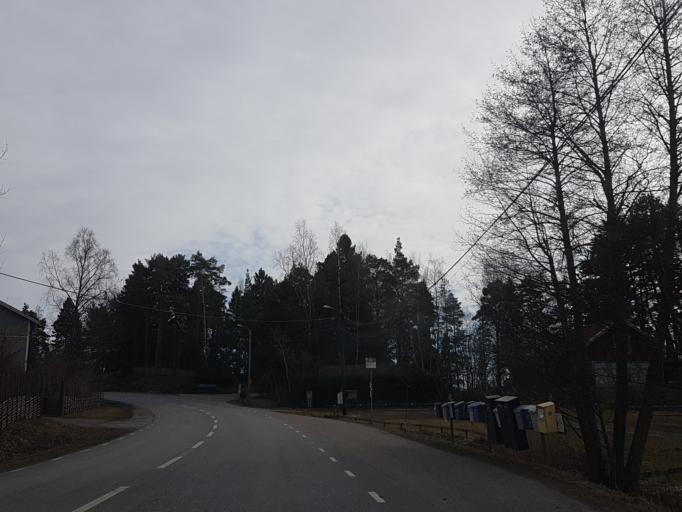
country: SE
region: Stockholm
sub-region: Norrtalje Kommun
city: Norrtalje
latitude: 59.6768
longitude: 18.7645
